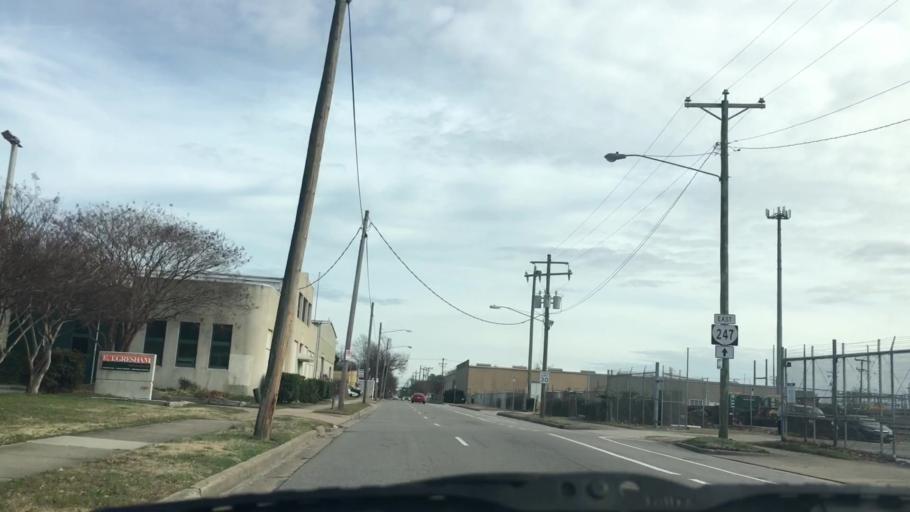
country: US
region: Virginia
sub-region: City of Norfolk
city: Norfolk
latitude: 36.8762
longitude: -76.3011
